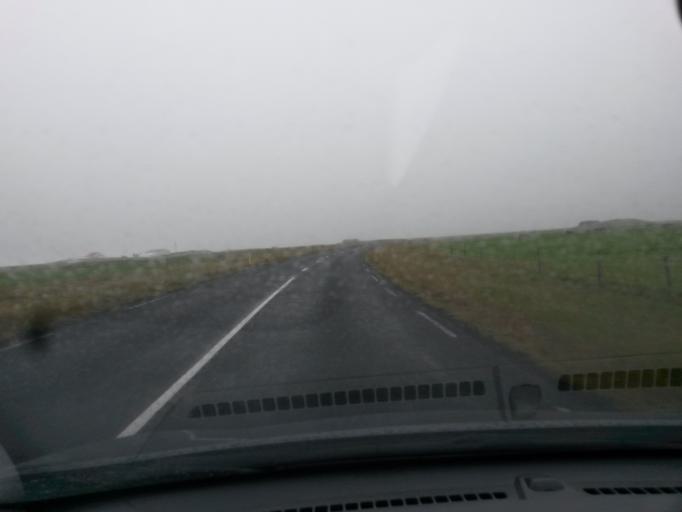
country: IS
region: South
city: Vestmannaeyjar
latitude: 63.4320
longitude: -19.1851
